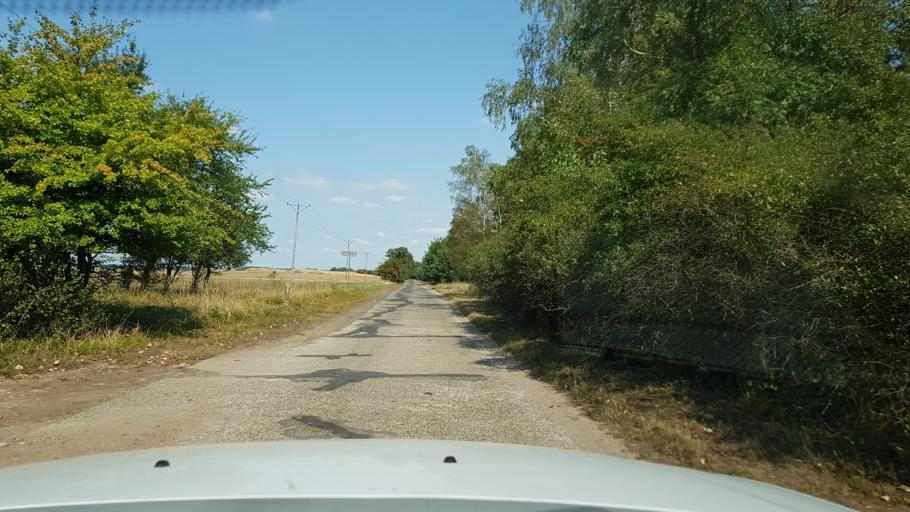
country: PL
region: West Pomeranian Voivodeship
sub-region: Powiat gryfinski
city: Moryn
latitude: 52.8301
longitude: 14.3700
